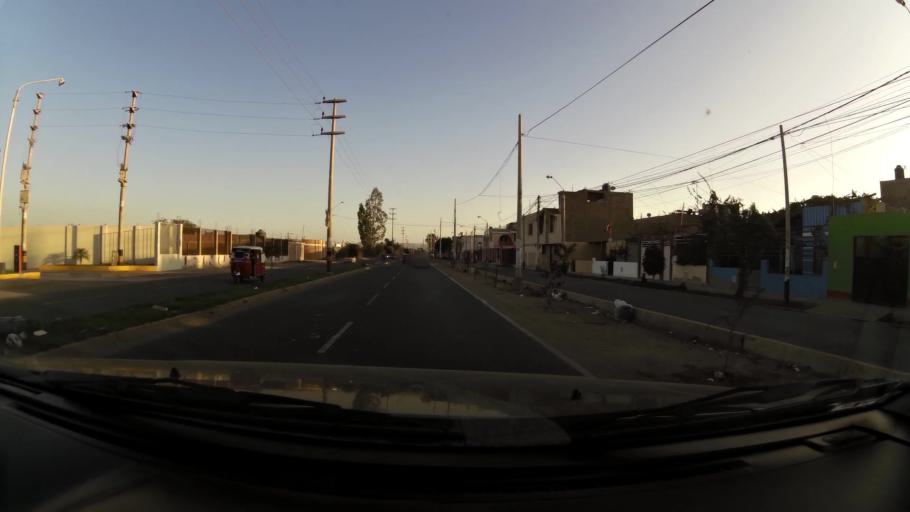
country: PE
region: Ica
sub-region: Provincia de Ica
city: Ica
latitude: -14.0839
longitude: -75.7224
